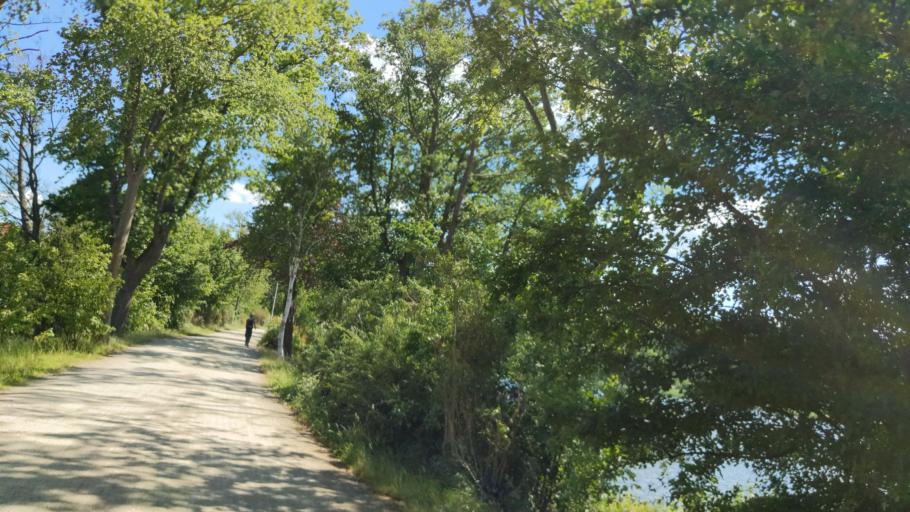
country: DE
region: Schleswig-Holstein
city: Ratzeburg
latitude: 53.6944
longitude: 10.7775
